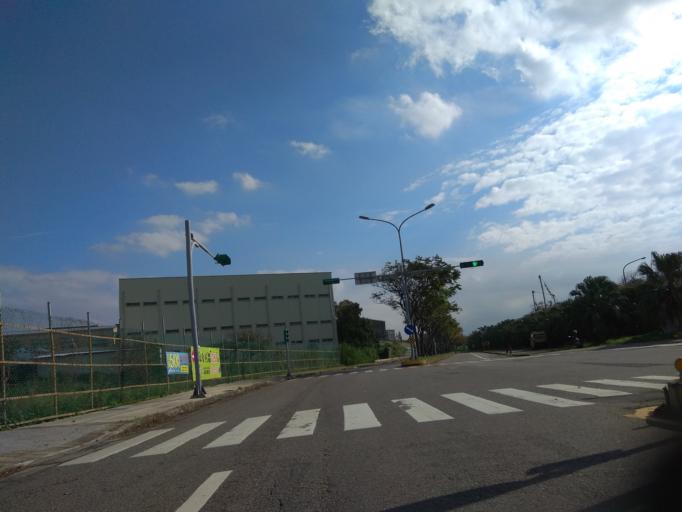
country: TW
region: Taiwan
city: Taoyuan City
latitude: 25.0587
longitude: 121.1797
